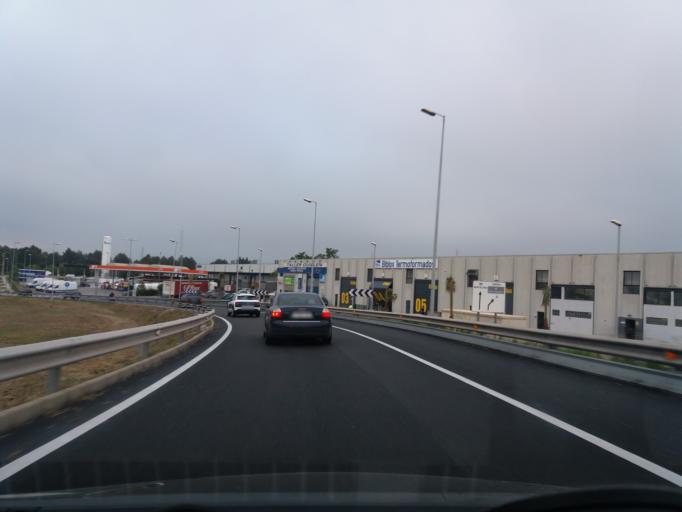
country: ES
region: Catalonia
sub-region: Provincia de Barcelona
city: Abrera
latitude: 41.5168
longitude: 1.8974
